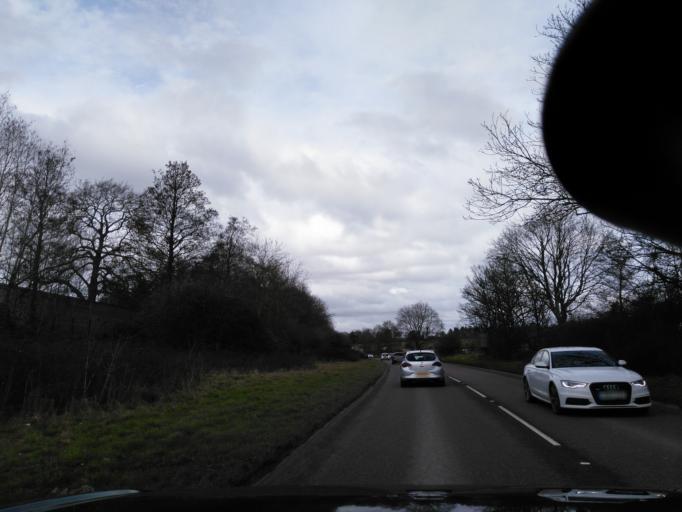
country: GB
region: England
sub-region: Wiltshire
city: Lacock
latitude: 51.4234
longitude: -2.1268
